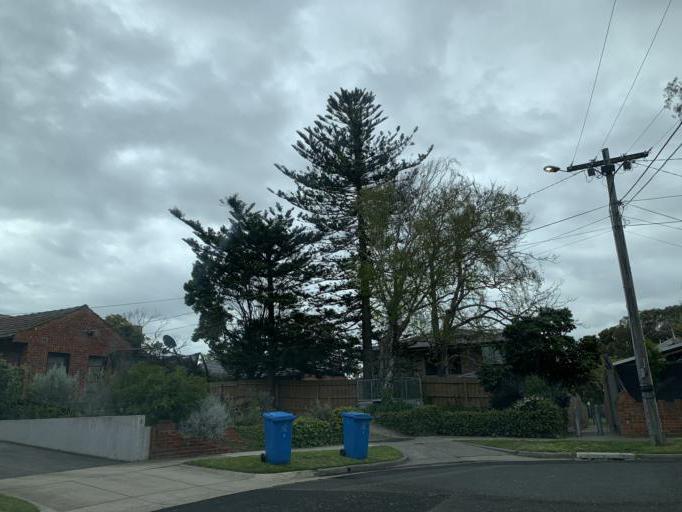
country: AU
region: Victoria
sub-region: Bayside
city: Black Rock
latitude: -37.9632
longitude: 145.0218
